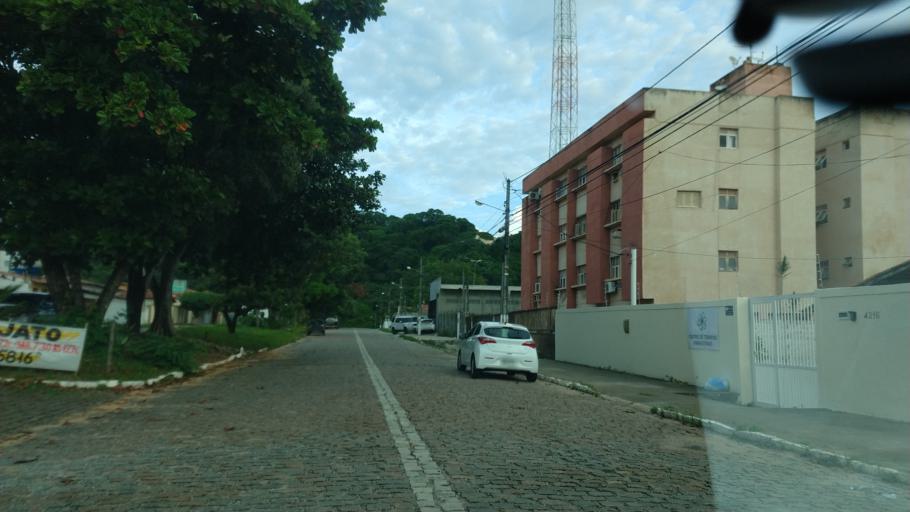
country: BR
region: Rio Grande do Norte
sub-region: Natal
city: Natal
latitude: -5.8180
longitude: -35.1993
